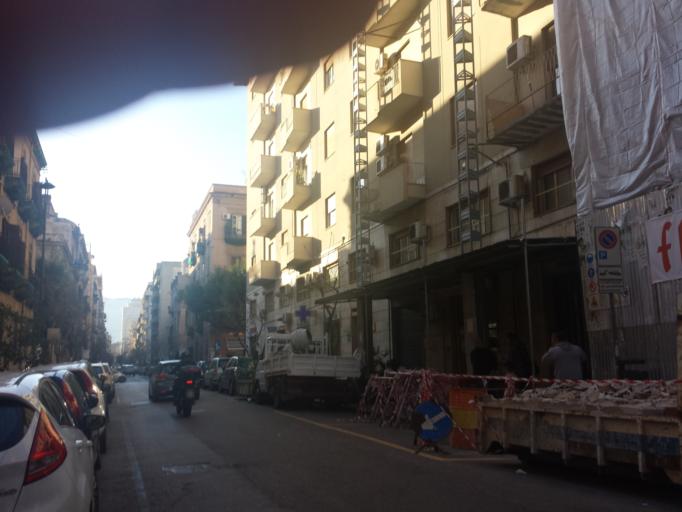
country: IT
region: Sicily
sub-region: Palermo
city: Palermo
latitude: 38.1279
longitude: 13.3512
